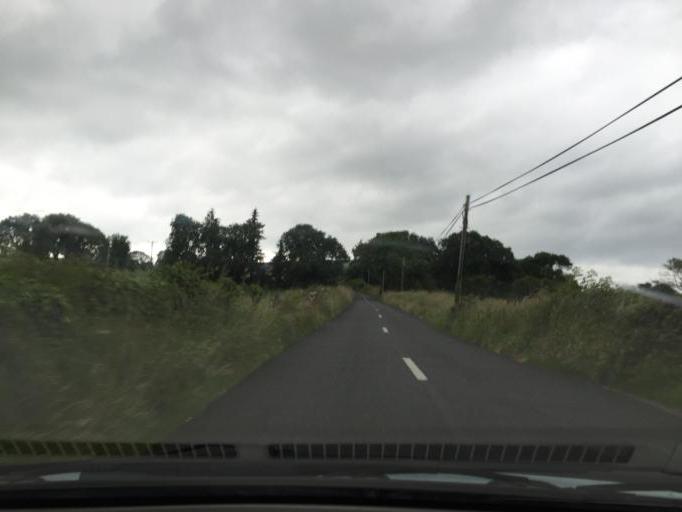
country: IE
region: Connaught
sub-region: Sligo
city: Sligo
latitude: 54.2635
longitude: -8.5196
